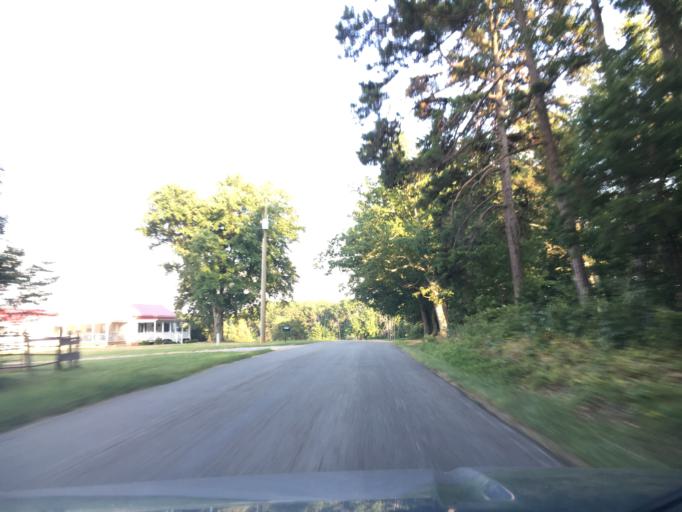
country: US
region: Virginia
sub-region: Halifax County
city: Mountain Road
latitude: 36.8384
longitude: -79.1510
